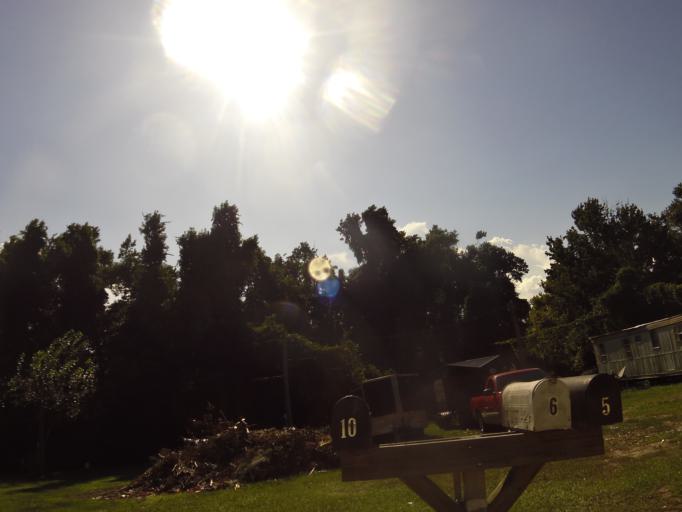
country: US
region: Florida
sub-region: Nassau County
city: Fernandina Beach
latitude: 30.6540
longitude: -81.4640
